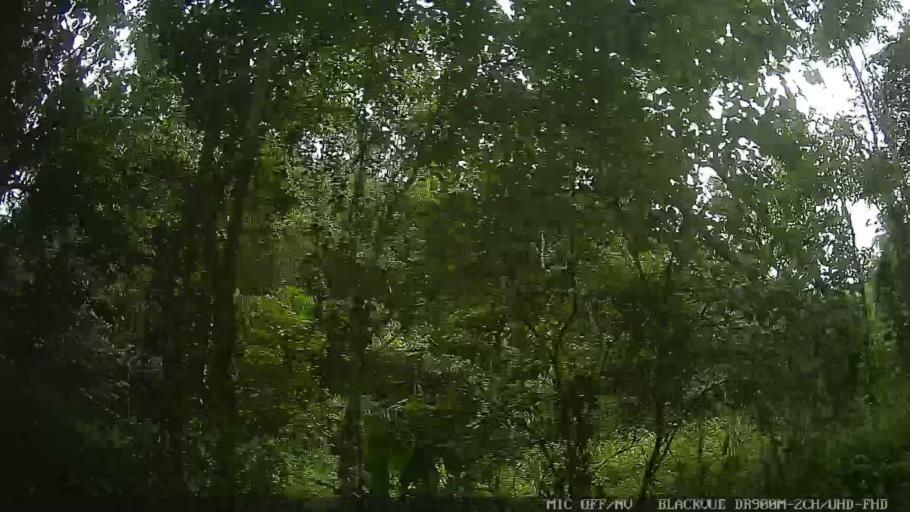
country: BR
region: Sao Paulo
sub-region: Aruja
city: Aruja
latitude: -23.4018
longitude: -46.2387
